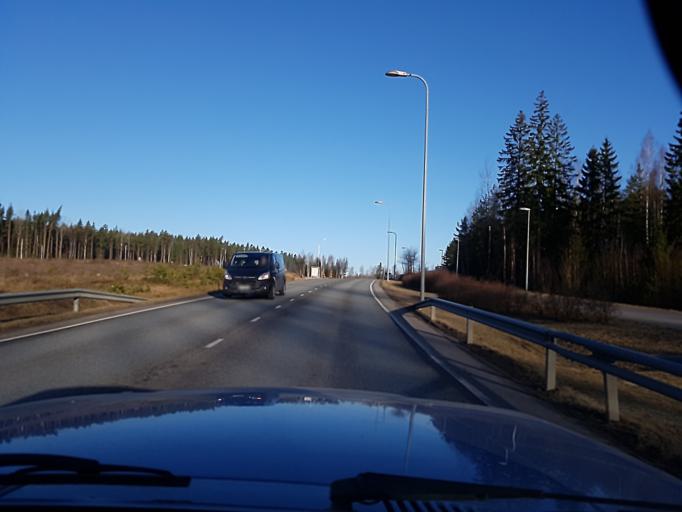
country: FI
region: Uusimaa
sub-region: Helsinki
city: Vantaa
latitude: 60.2912
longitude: 24.9333
